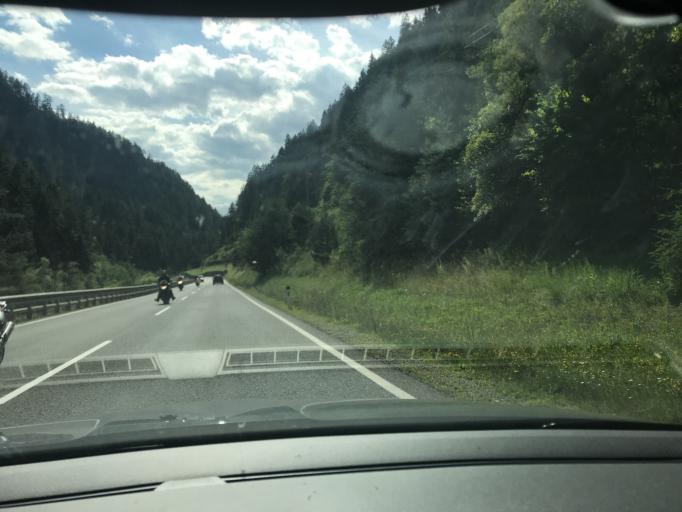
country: AT
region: Tyrol
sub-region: Politischer Bezirk Lienz
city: Leisach
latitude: 46.7875
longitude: 12.6966
